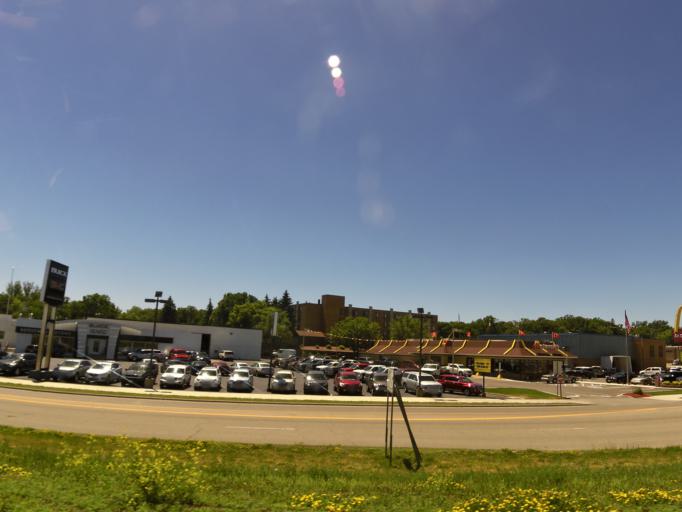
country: US
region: Minnesota
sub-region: Becker County
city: Detroit Lakes
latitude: 46.8157
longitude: -95.8370
